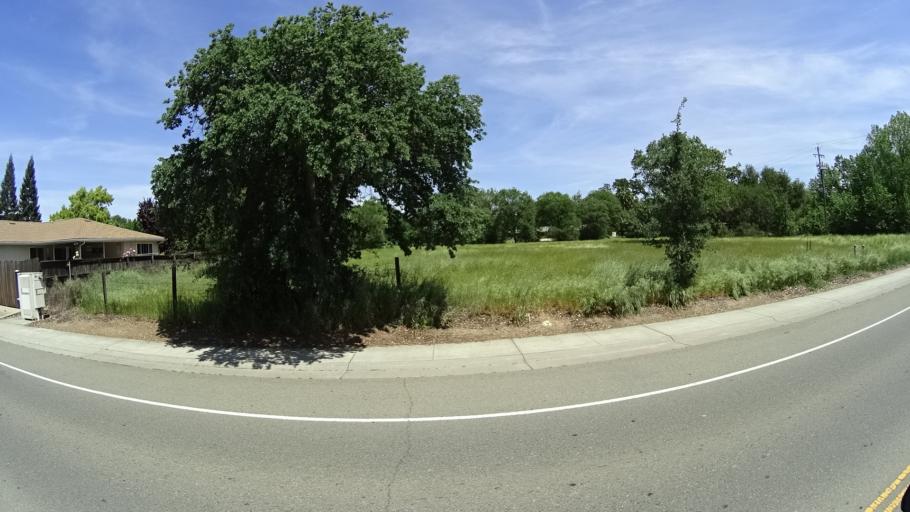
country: US
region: California
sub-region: Placer County
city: Rocklin
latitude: 38.7968
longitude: -121.2364
